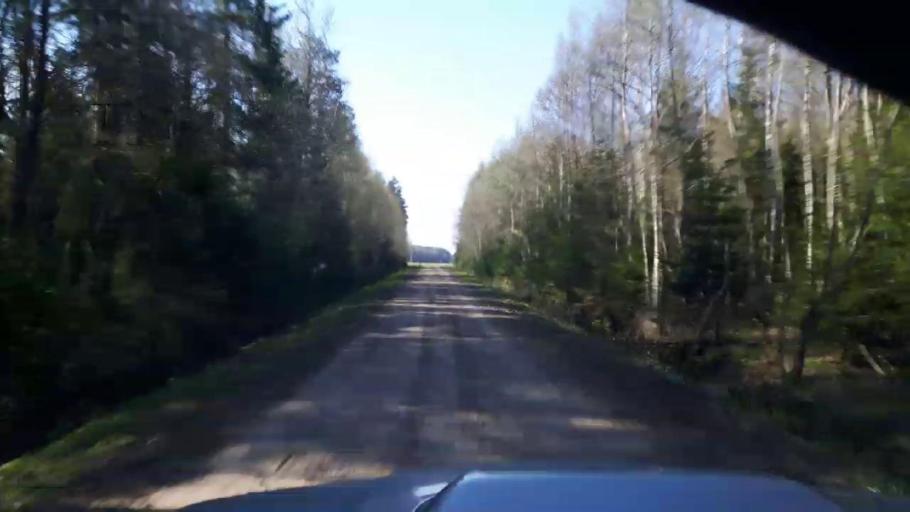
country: EE
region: Paernumaa
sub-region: Tootsi vald
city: Tootsi
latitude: 58.5147
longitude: 24.9283
